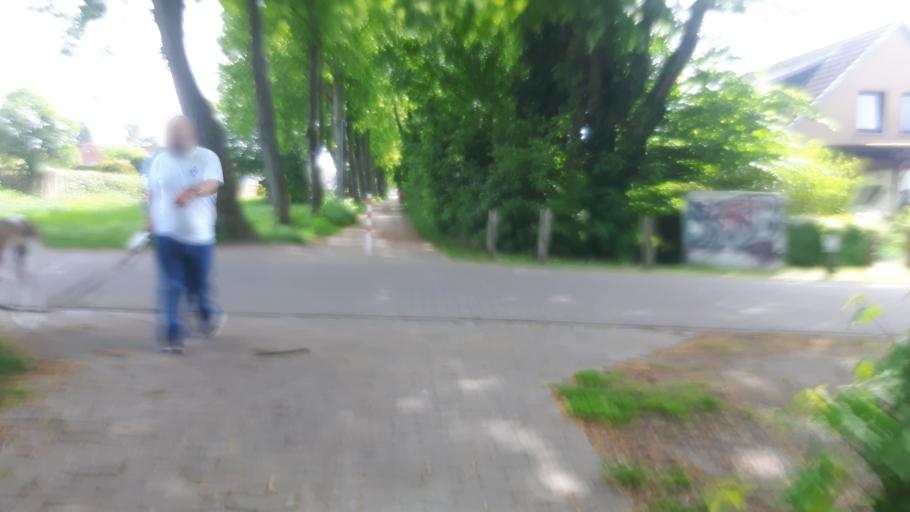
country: DE
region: Lower Saxony
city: Stuhr
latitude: 53.0637
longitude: 8.7603
